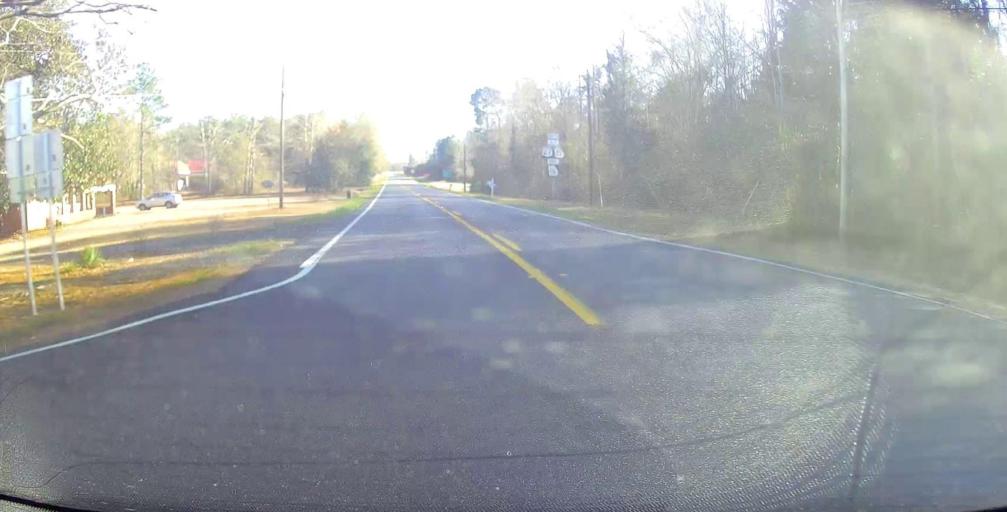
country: US
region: Georgia
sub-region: Talbot County
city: Sardis
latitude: 32.8046
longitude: -84.6956
